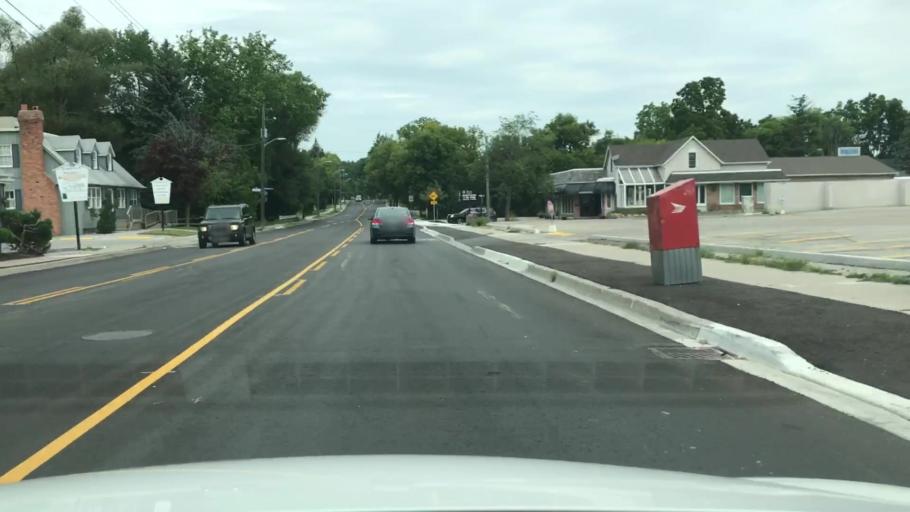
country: CA
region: Ontario
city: Newmarket
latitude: 44.0597
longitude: -79.4614
